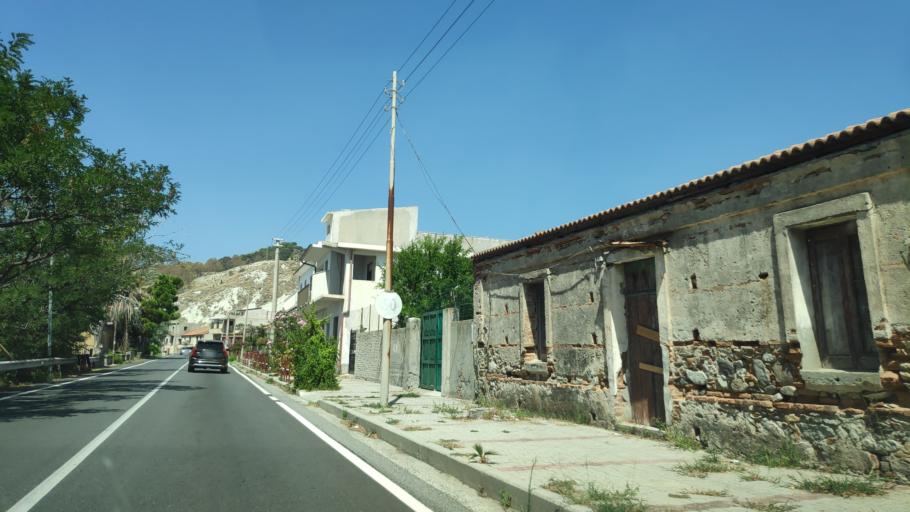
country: IT
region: Calabria
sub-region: Provincia di Reggio Calabria
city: Palizzi Marina
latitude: 37.9238
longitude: 16.0414
